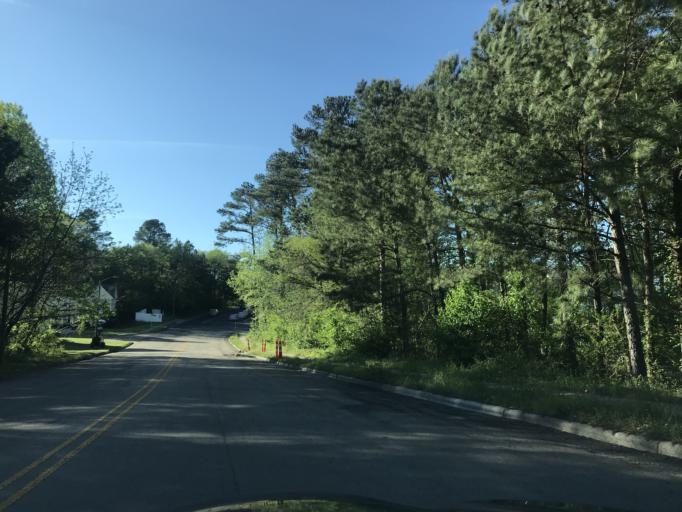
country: US
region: North Carolina
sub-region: Wake County
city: Raleigh
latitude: 35.8434
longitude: -78.5678
